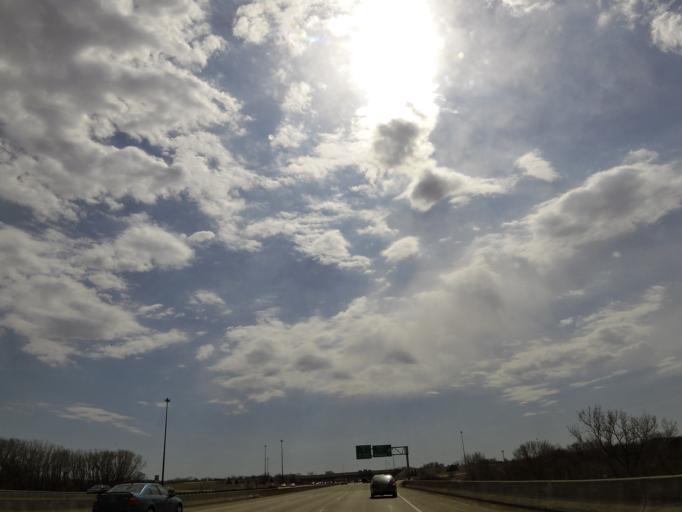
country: US
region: Minnesota
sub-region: Dakota County
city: Eagan
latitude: 44.8200
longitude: -93.2243
